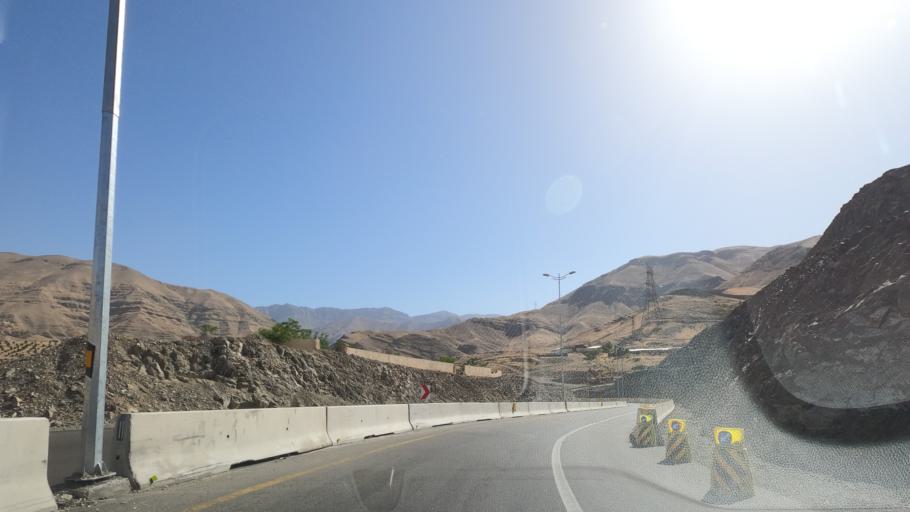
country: IR
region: Alborz
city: Karaj
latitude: 35.8218
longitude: 51.0378
